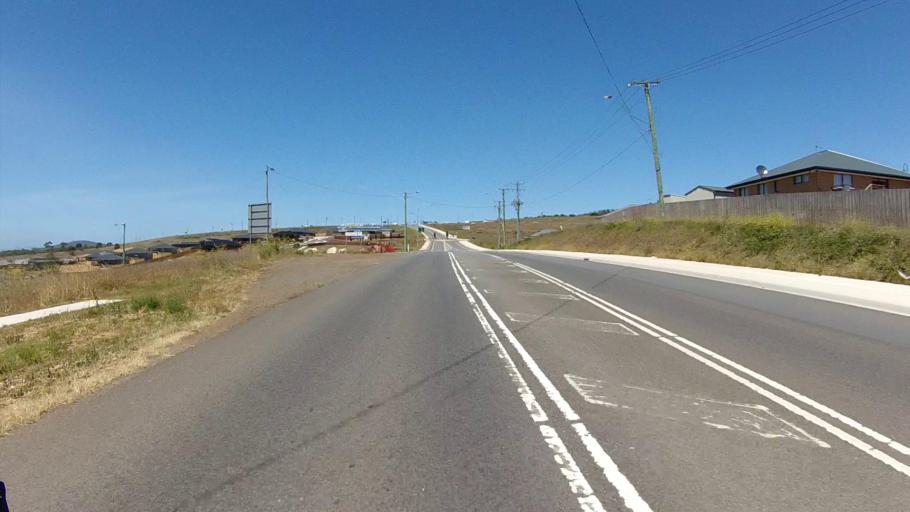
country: AU
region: Tasmania
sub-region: Clarence
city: Howrah
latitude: -42.8844
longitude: 147.4285
